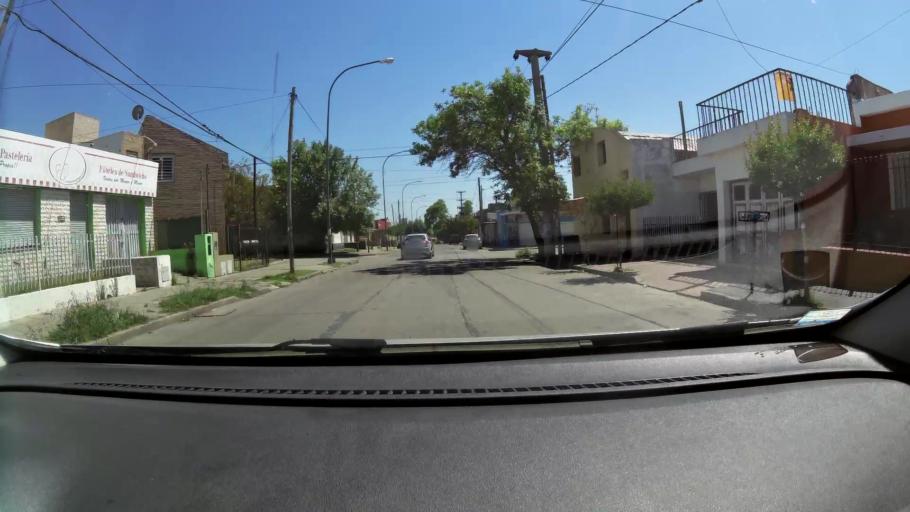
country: AR
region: Cordoba
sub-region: Departamento de Capital
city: Cordoba
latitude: -31.4231
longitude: -64.2093
